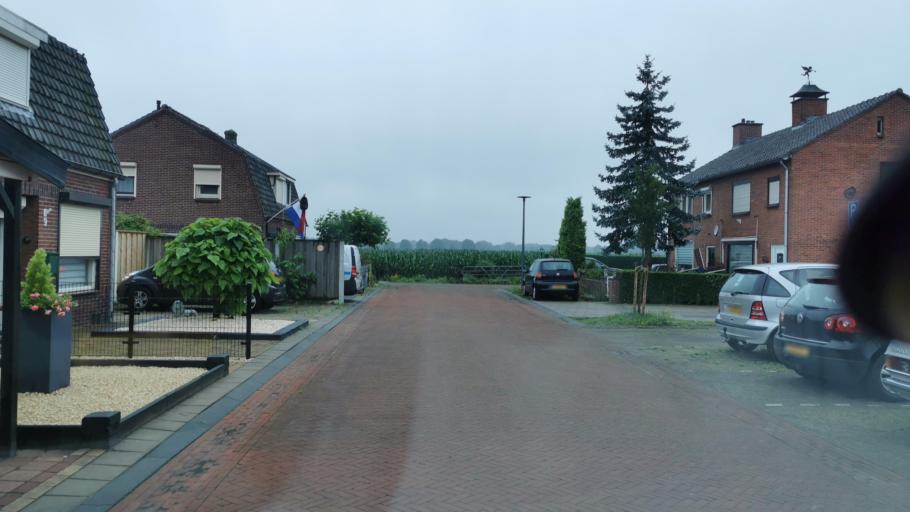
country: NL
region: Overijssel
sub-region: Gemeente Losser
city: Losser
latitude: 52.2422
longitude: 7.0300
